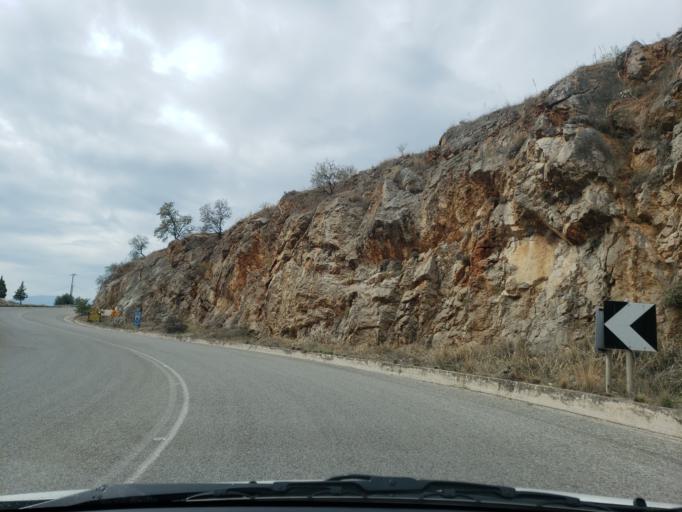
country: GR
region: Central Greece
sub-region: Nomos Fokidos
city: Delphi
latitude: 38.4725
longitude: 22.4651
